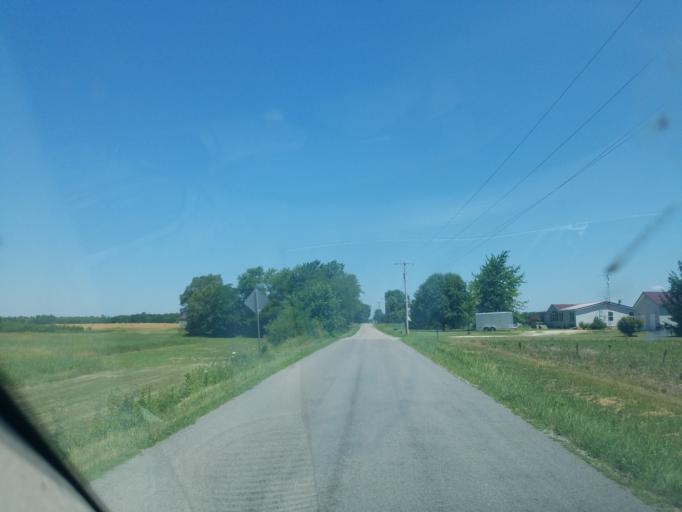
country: US
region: Ohio
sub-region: Mercer County
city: Rockford
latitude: 40.7276
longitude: -84.7370
